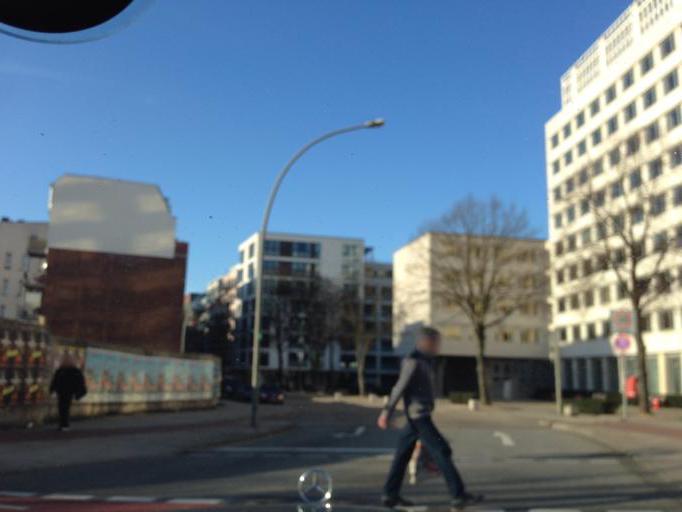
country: DE
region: Hamburg
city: Hamburg-Mitte
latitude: 53.5530
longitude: 10.0193
